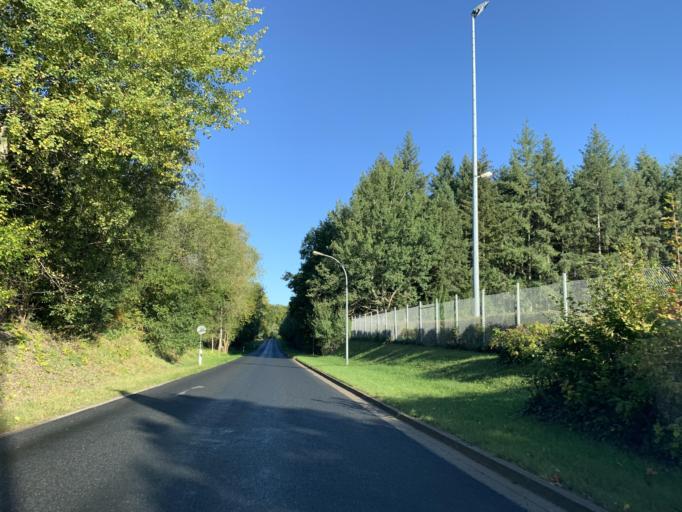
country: DE
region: Mecklenburg-Vorpommern
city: Burg Stargard
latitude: 53.5084
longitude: 13.2627
